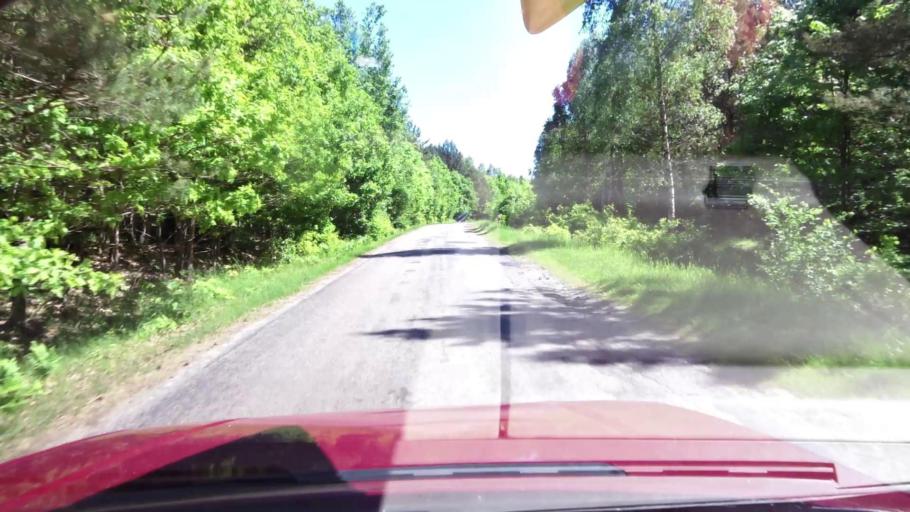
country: PL
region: West Pomeranian Voivodeship
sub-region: Powiat koszalinski
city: Bobolice
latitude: 54.0706
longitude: 16.5091
